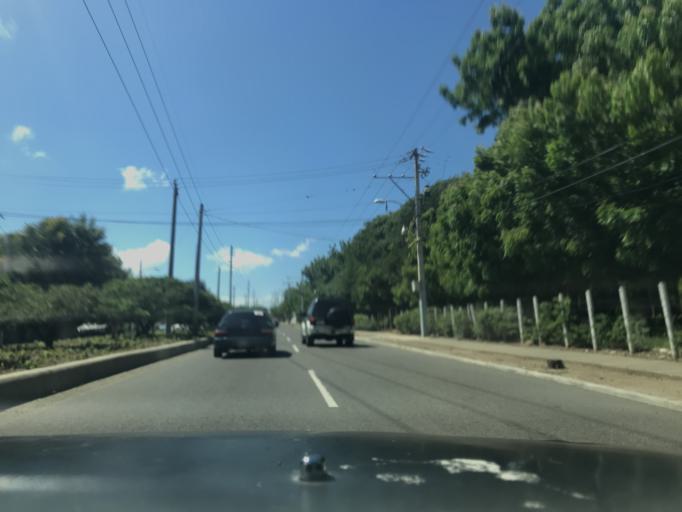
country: DO
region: Santiago
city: Santiago de los Caballeros
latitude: 19.4499
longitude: -70.7441
